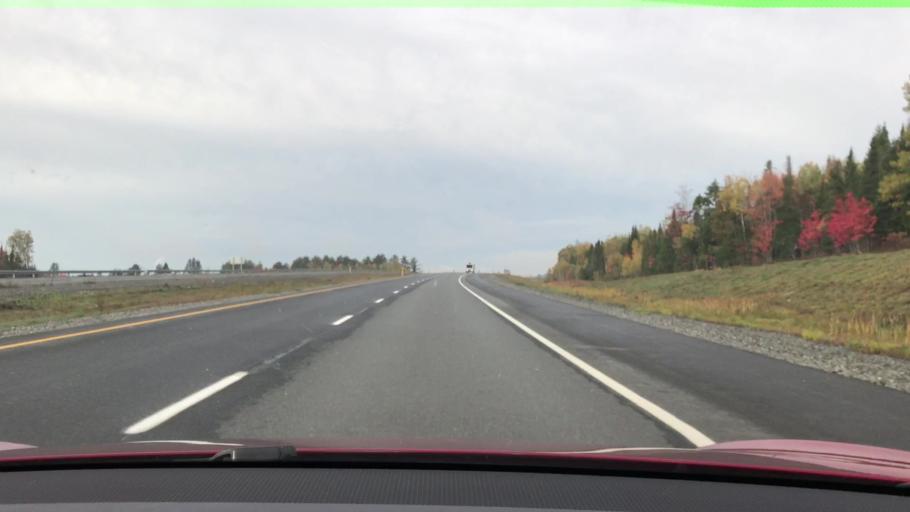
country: US
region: Maine
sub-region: Washington County
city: Calais
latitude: 45.2143
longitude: -67.2506
